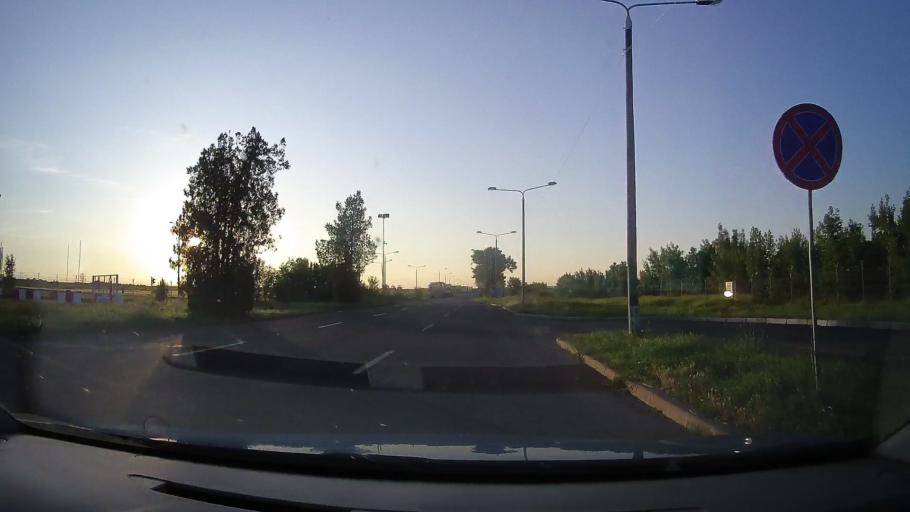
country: RO
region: Timis
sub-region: Comuna Moravita
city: Moravita
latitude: 45.2339
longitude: 21.2713
